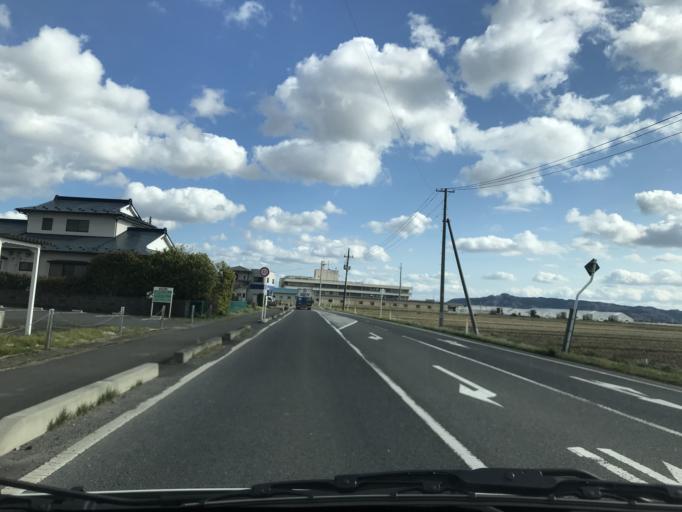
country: JP
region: Miyagi
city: Wakuya
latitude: 38.6319
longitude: 141.1885
